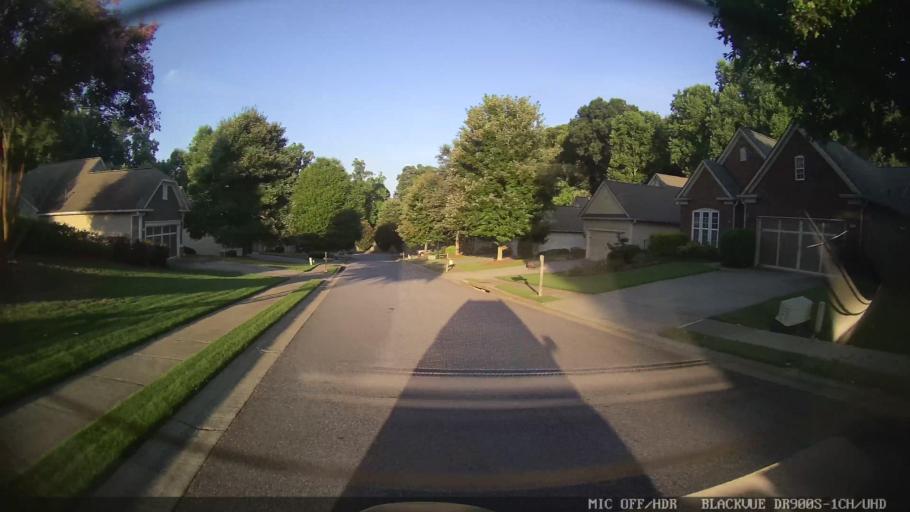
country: US
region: Georgia
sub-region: Forsyth County
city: Cumming
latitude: 34.2156
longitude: -84.2363
